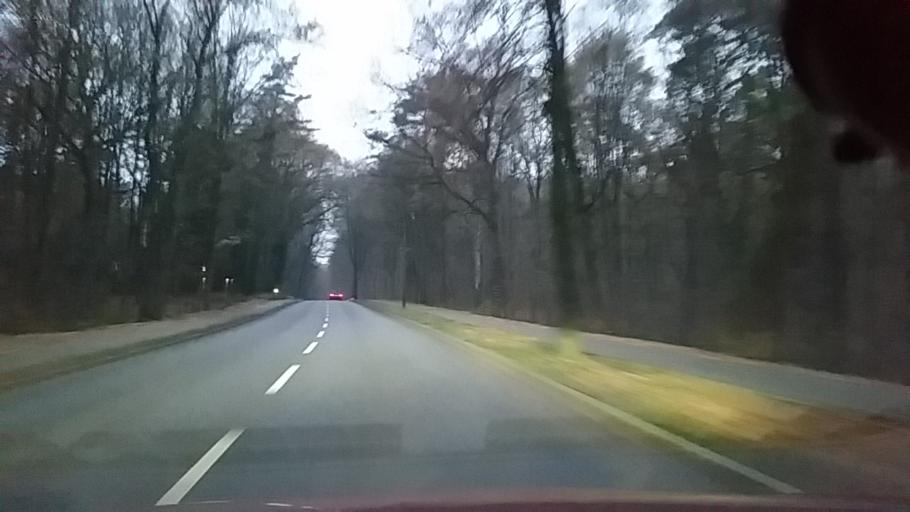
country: DE
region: Schleswig-Holstein
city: Rellingen
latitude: 53.5723
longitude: 9.7867
